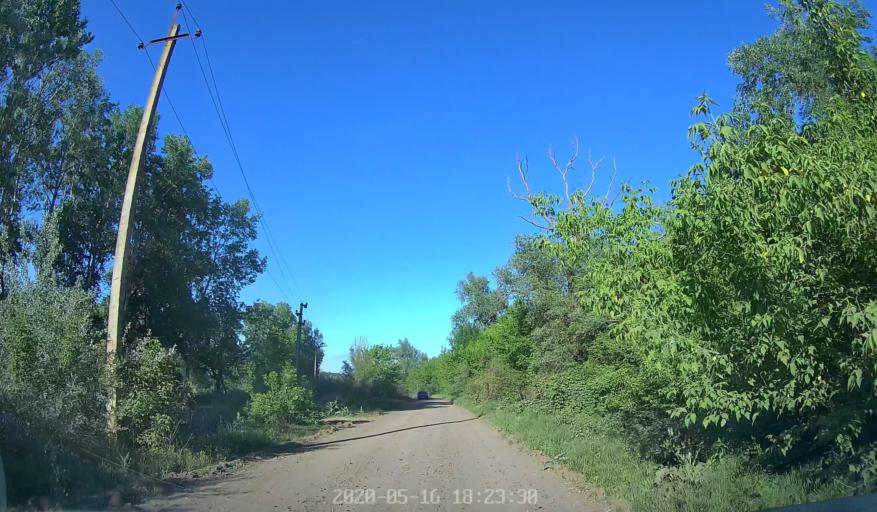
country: MD
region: Telenesti
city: Dnestrovsc
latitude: 46.5422
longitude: 29.9903
